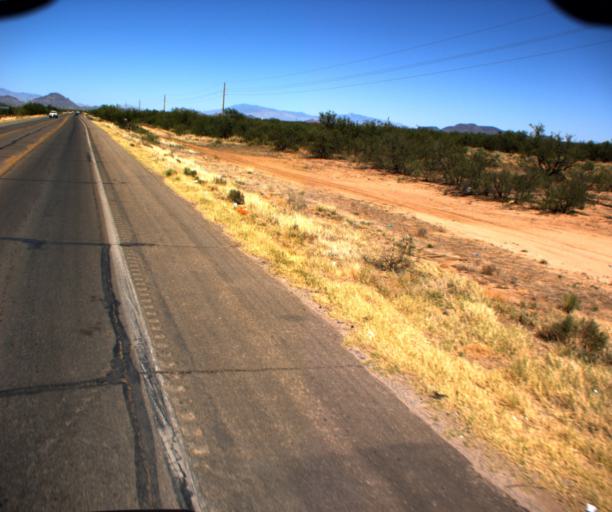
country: US
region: Arizona
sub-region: Pima County
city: Three Points
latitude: 32.1116
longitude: -111.2259
